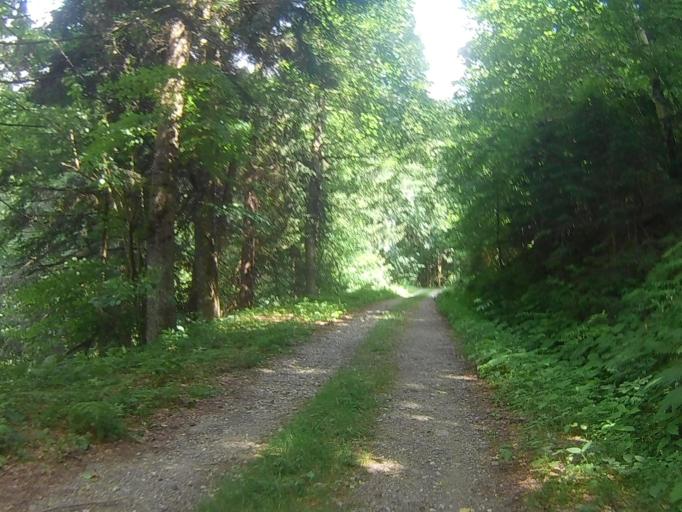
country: SI
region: Ruse
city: Ruse
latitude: 46.5122
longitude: 15.5271
